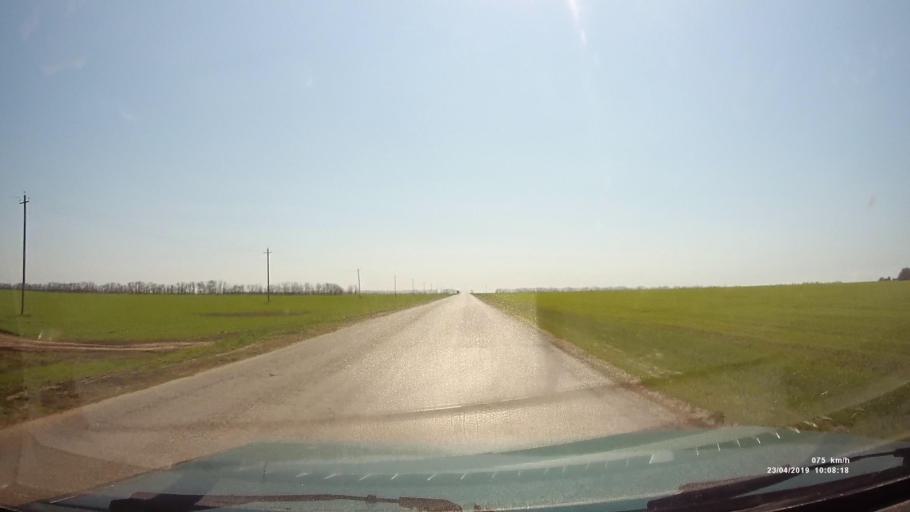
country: RU
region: Rostov
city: Sovetskoye
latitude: 46.7203
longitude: 42.2635
